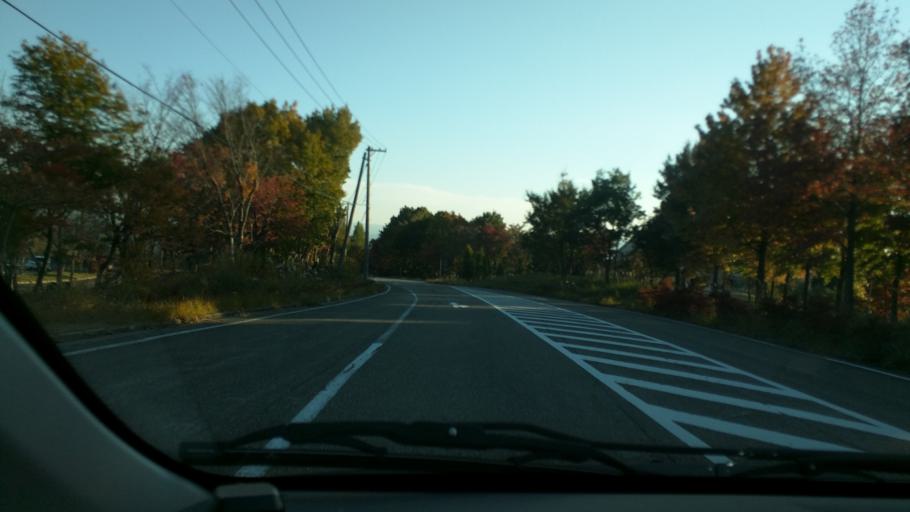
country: JP
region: Fukushima
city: Inawashiro
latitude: 37.5803
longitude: 140.0267
